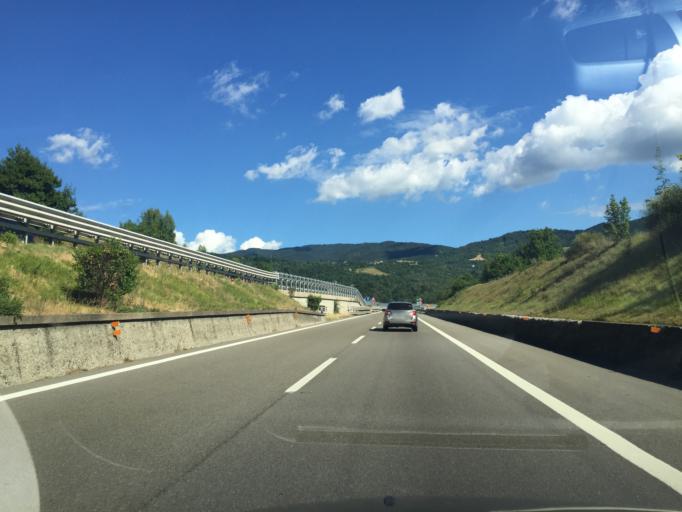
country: IT
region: Emilia-Romagna
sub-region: Provincia di Parma
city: Berceto
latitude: 44.5191
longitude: 9.9594
